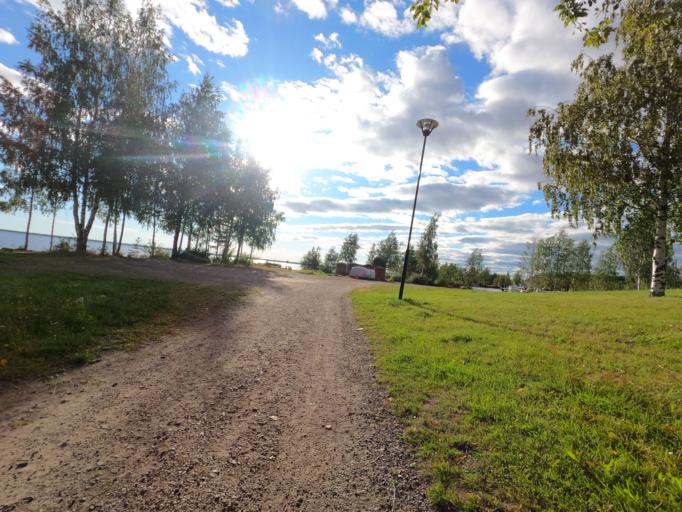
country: FI
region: North Karelia
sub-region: Joensuu
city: Joensuu
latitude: 62.5944
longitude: 29.7313
